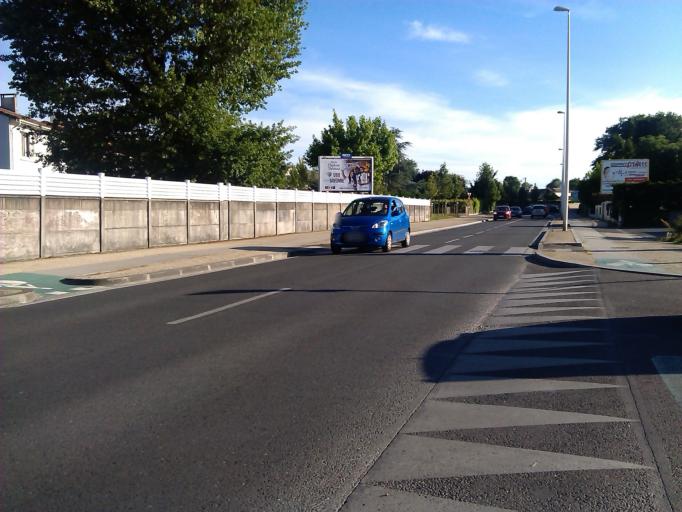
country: FR
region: Aquitaine
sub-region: Departement de la Gironde
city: Pessac
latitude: 44.7908
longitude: -0.6731
